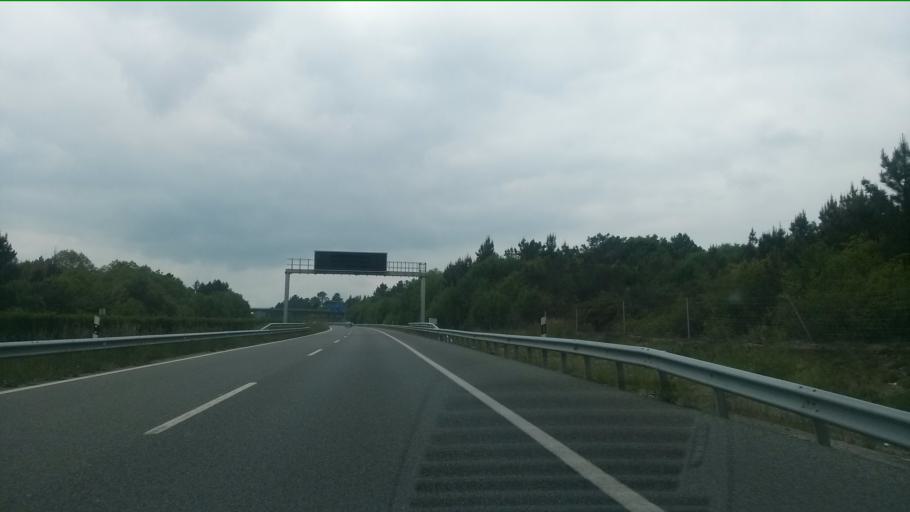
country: ES
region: Galicia
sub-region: Provincia de Lugo
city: Guitiriz
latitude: 43.1898
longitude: -7.9346
